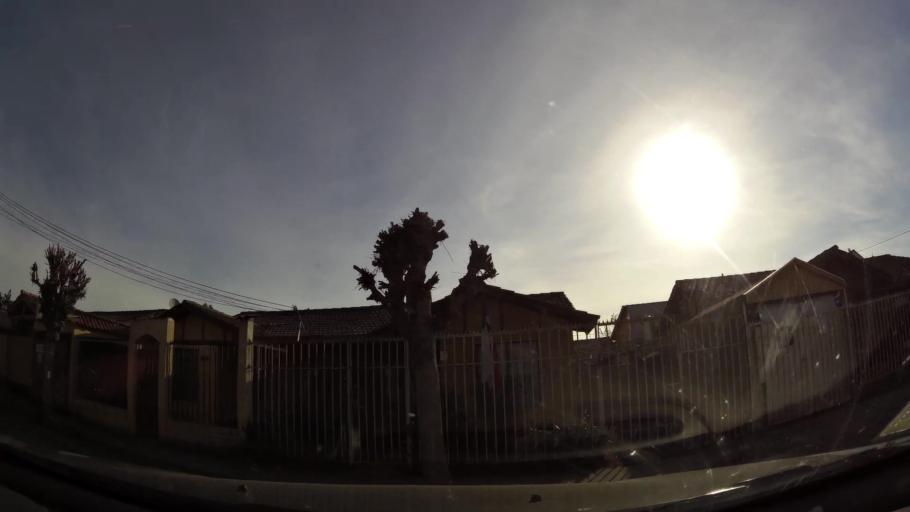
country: CL
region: Santiago Metropolitan
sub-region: Provincia de Cordillera
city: Puente Alto
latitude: -33.5858
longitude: -70.5646
